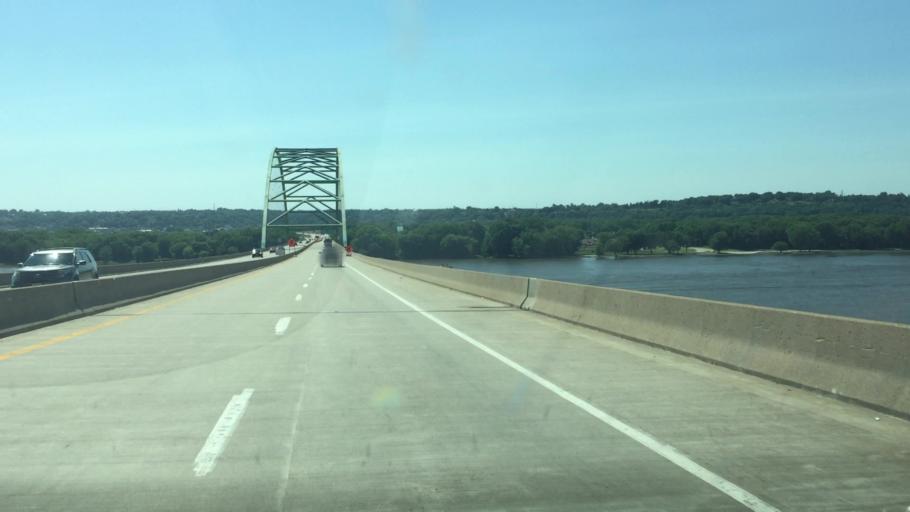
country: US
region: Illinois
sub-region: Jo Daviess County
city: East Dubuque
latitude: 42.5155
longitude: -90.6312
